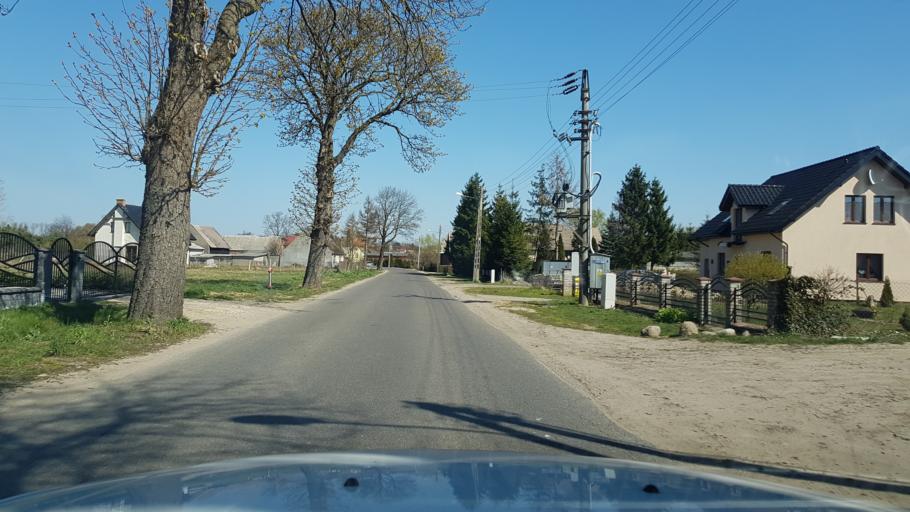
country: PL
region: West Pomeranian Voivodeship
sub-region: Powiat slawienski
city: Slawno
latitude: 54.3884
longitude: 16.7008
